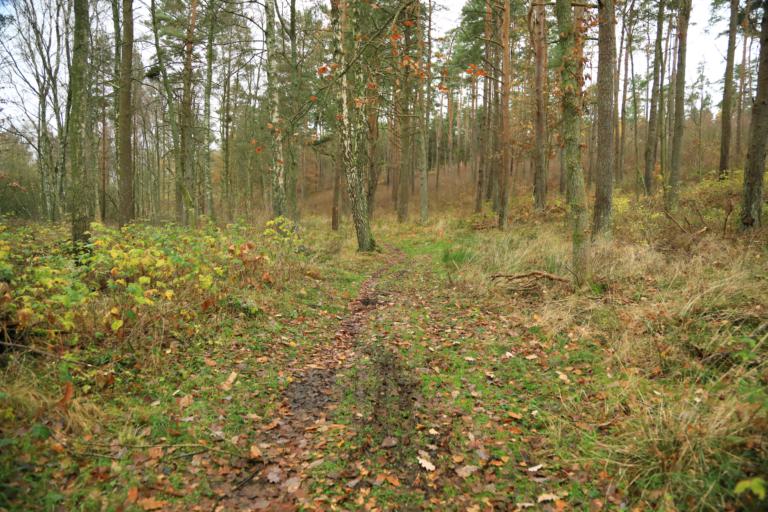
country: SE
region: Halland
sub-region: Varbergs Kommun
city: Varberg
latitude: 57.1759
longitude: 12.2128
